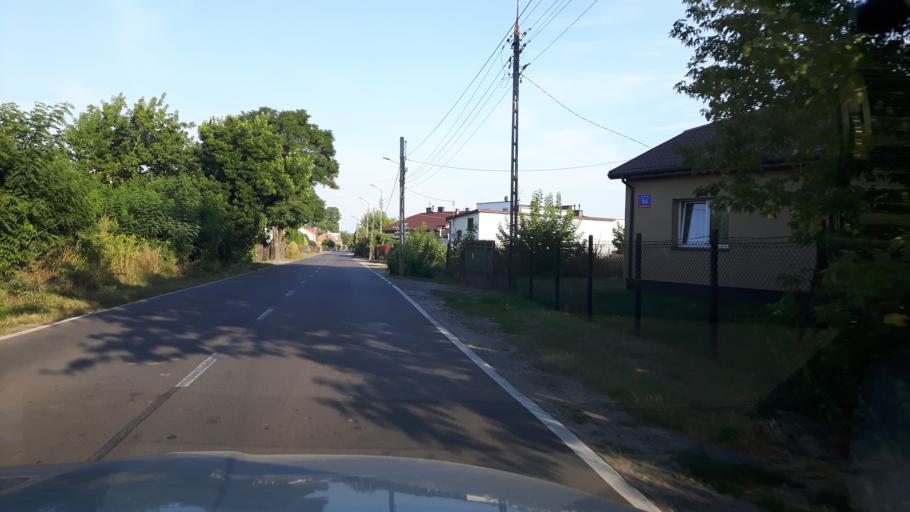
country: PL
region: Masovian Voivodeship
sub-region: Powiat wolominski
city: Slupno
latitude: 52.3629
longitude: 21.1624
